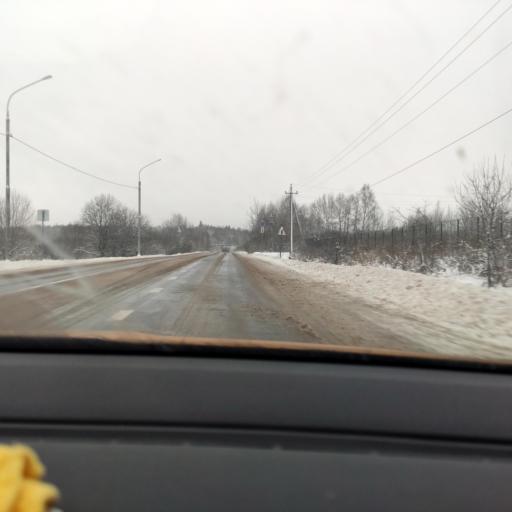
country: RU
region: Moskovskaya
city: Yershovo
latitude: 55.7591
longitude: 36.8680
